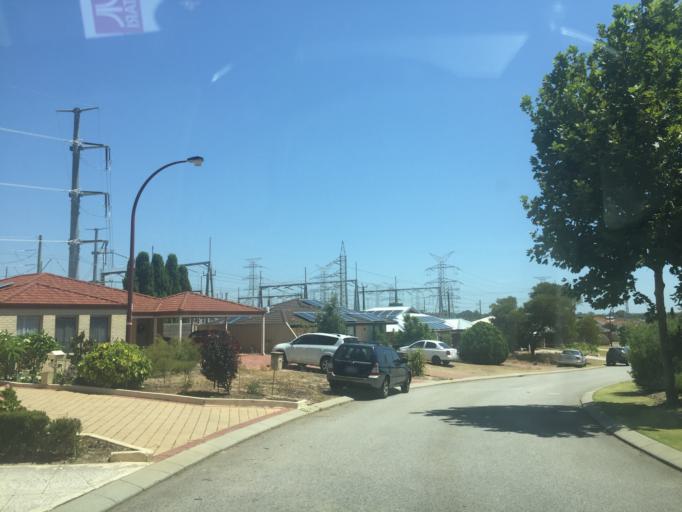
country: AU
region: Western Australia
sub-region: City of Cockburn
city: City of Cockburn
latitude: -32.0936
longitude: 115.8442
